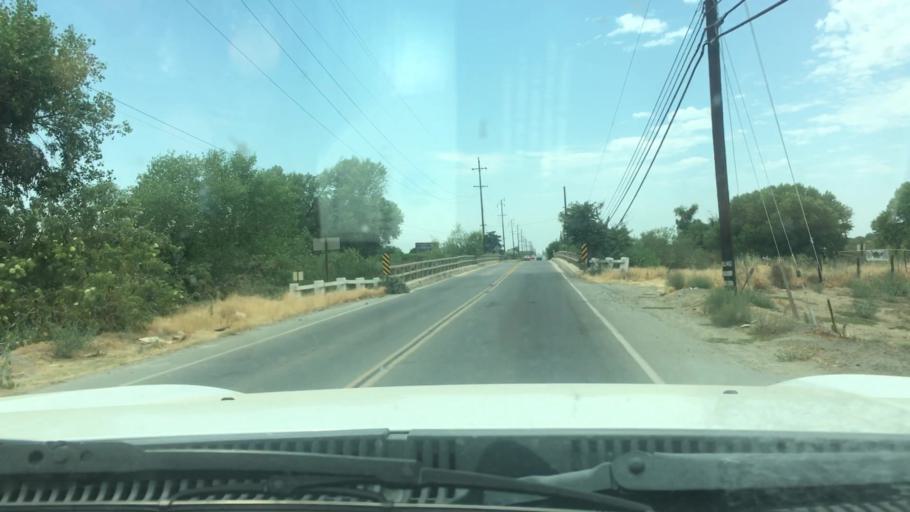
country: US
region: California
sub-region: Tulare County
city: Porterville
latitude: 36.0659
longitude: -119.0801
